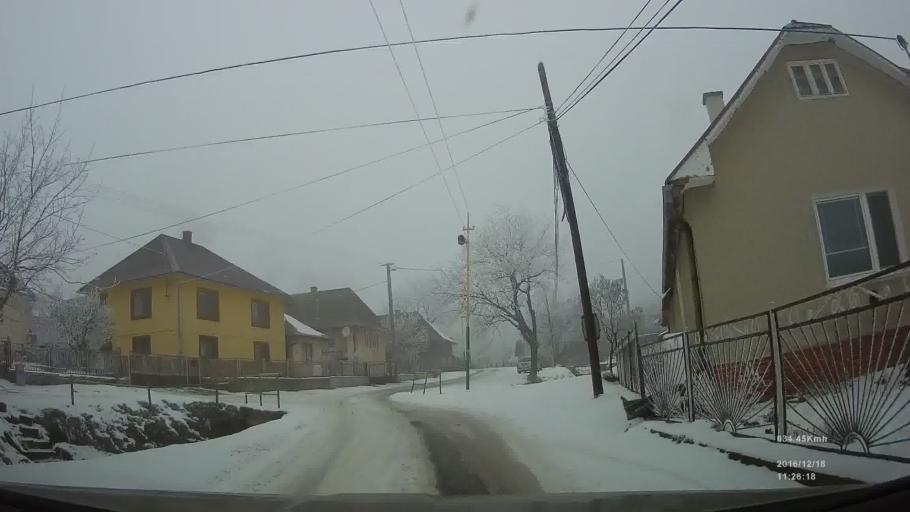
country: SK
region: Presovsky
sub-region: Okres Presov
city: Presov
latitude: 48.8998
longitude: 21.4076
